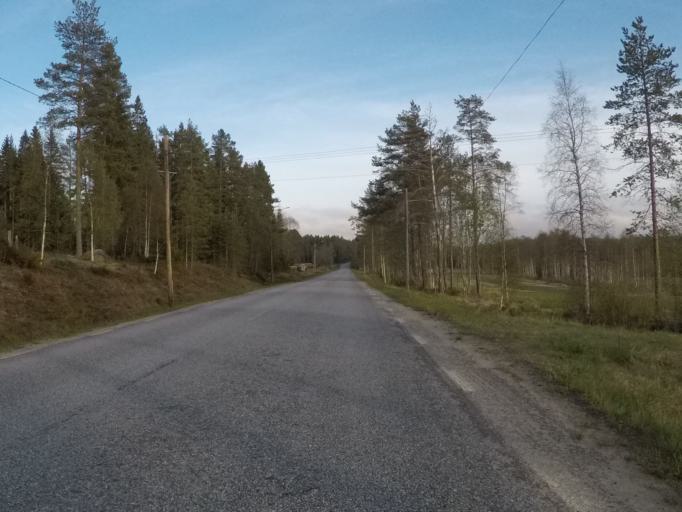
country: SE
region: Vaesterbotten
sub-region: Robertsfors Kommun
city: Robertsfors
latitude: 63.9951
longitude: 20.8077
